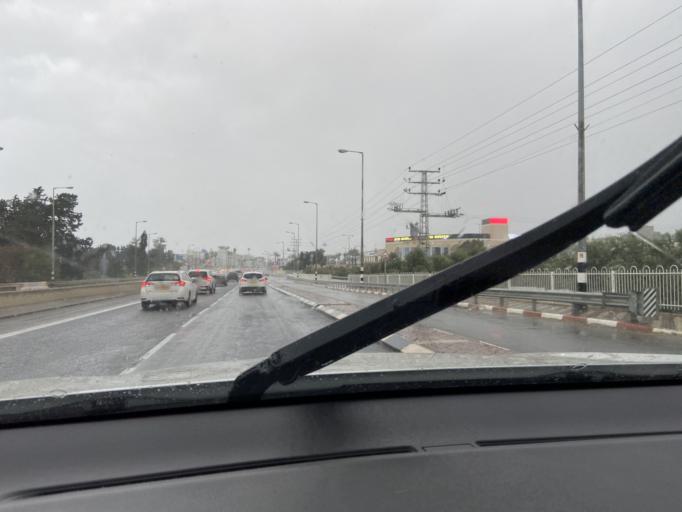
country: IL
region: Northern District
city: El Mazra`a
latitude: 32.9850
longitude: 35.0953
